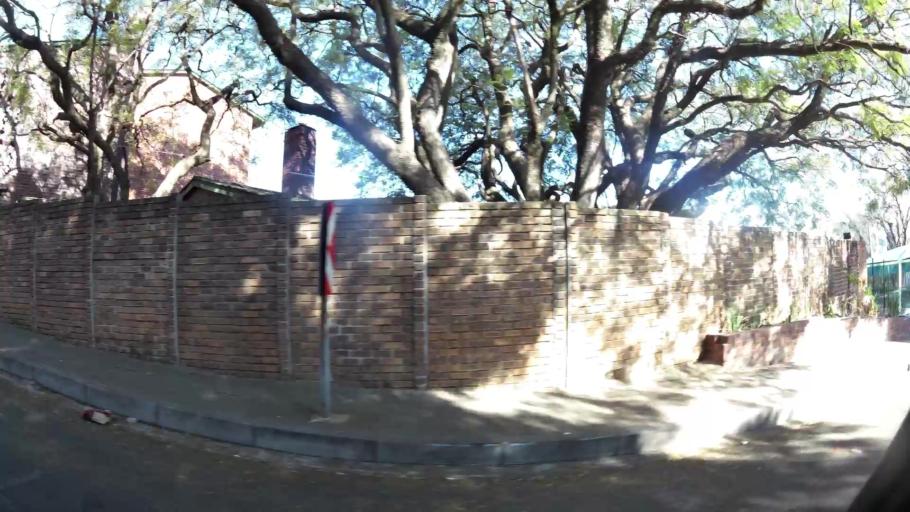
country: ZA
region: Gauteng
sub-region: City of Johannesburg Metropolitan Municipality
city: Johannesburg
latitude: -26.1222
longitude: 28.0249
